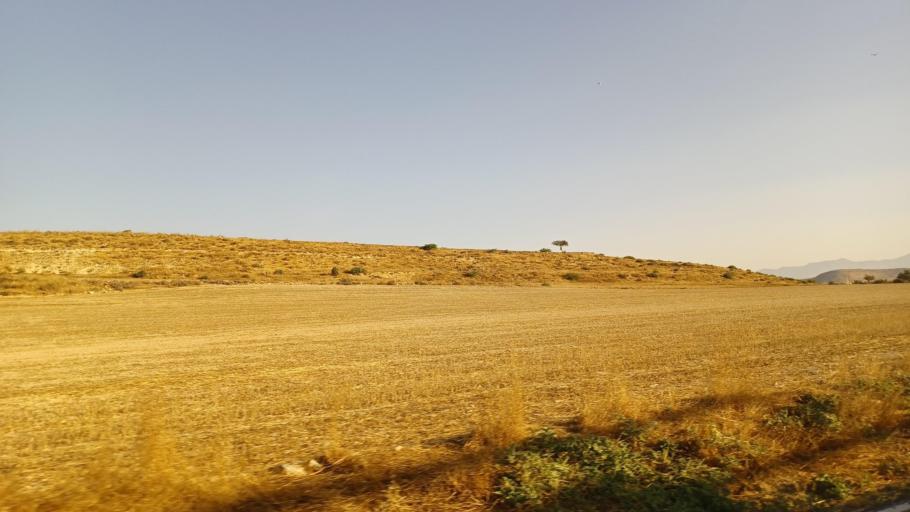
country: CY
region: Larnaka
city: Athienou
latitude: 35.0437
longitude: 33.5164
